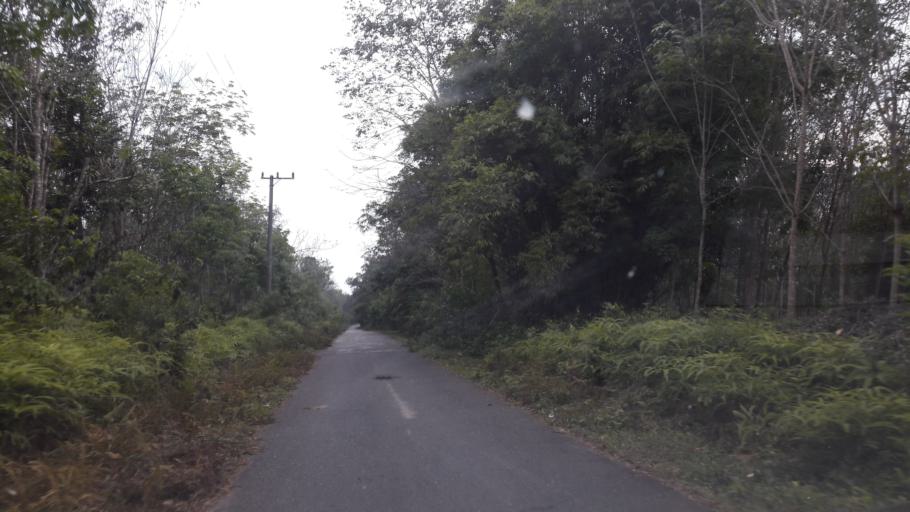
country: ID
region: South Sumatra
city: Gunungmenang
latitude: -3.1040
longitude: 104.0597
